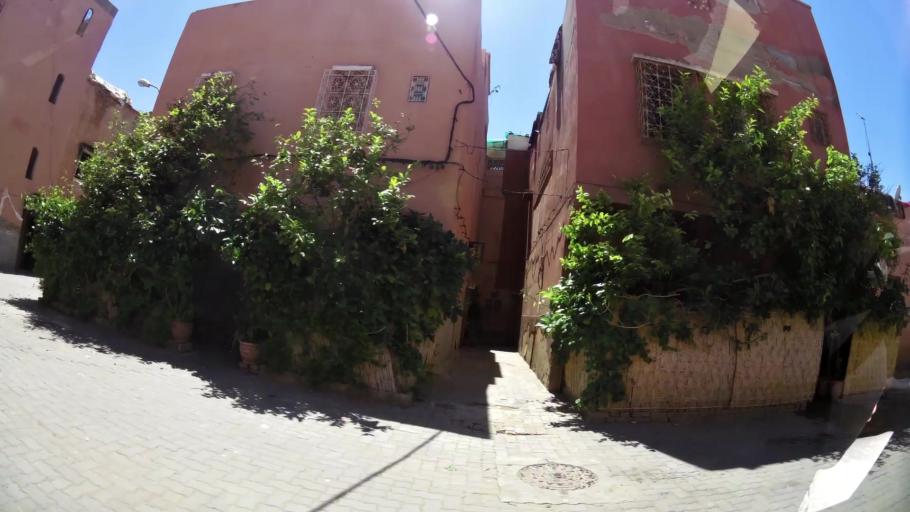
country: MA
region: Marrakech-Tensift-Al Haouz
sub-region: Marrakech
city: Marrakesh
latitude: 31.6297
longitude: -8.0432
